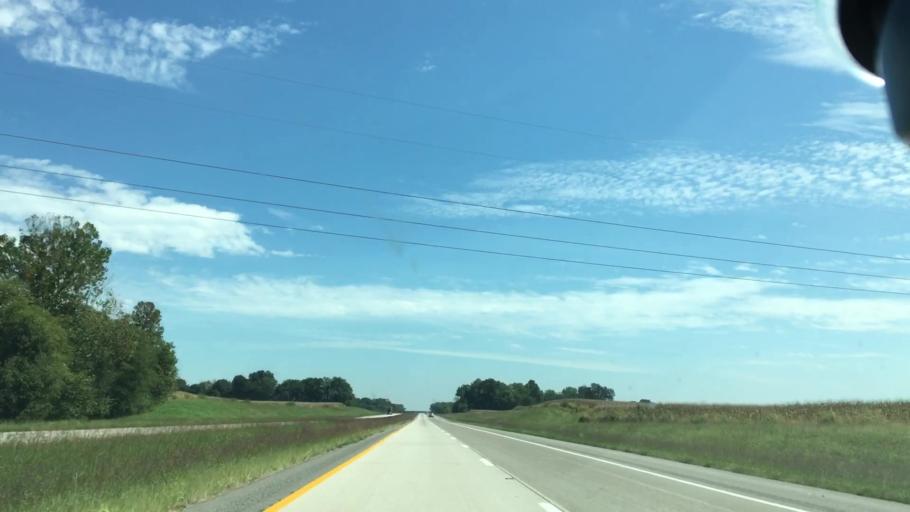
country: US
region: Kentucky
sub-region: Henderson County
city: Henderson
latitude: 37.7991
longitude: -87.5108
